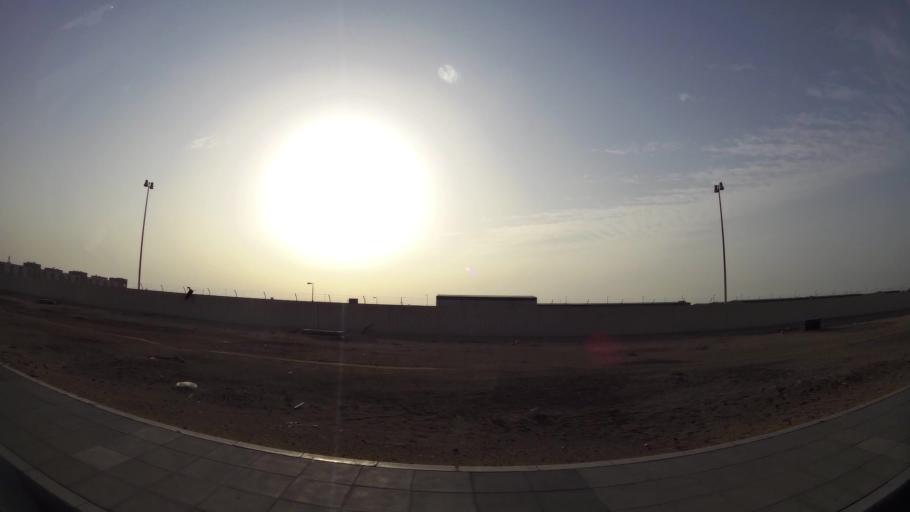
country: AE
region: Abu Dhabi
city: Abu Dhabi
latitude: 24.3512
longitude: 54.5120
